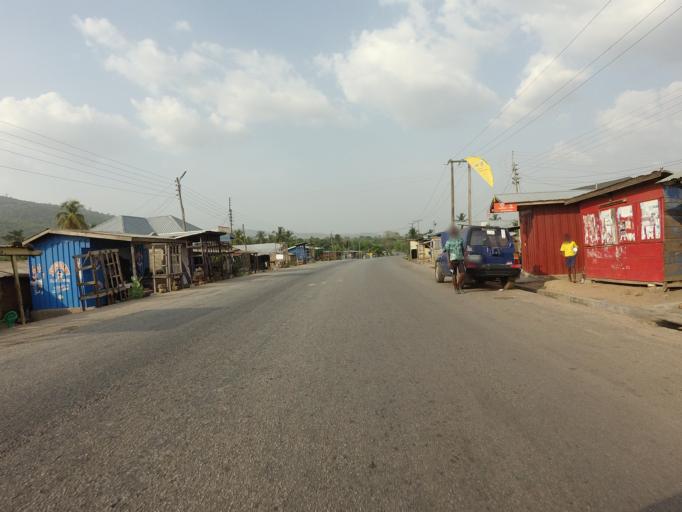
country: GH
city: Akropong
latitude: 6.2574
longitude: 0.1346
